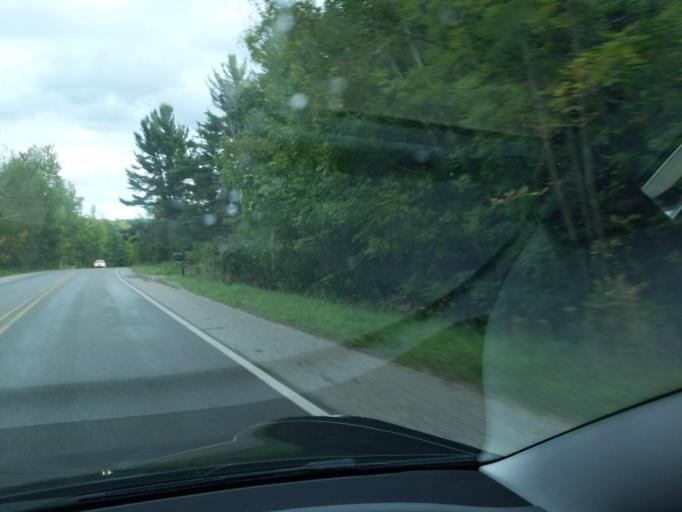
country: US
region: Michigan
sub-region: Kalkaska County
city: Rapid City
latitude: 44.8032
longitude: -85.2755
